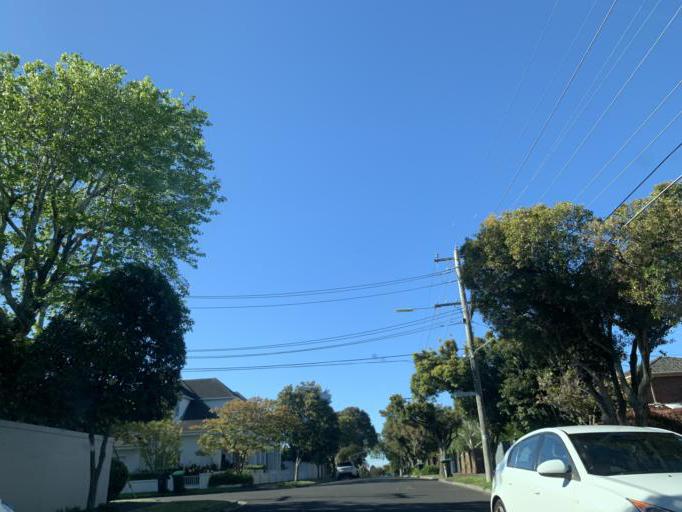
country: AU
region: Victoria
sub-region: Bayside
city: Hampton
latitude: -37.9245
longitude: 144.9962
